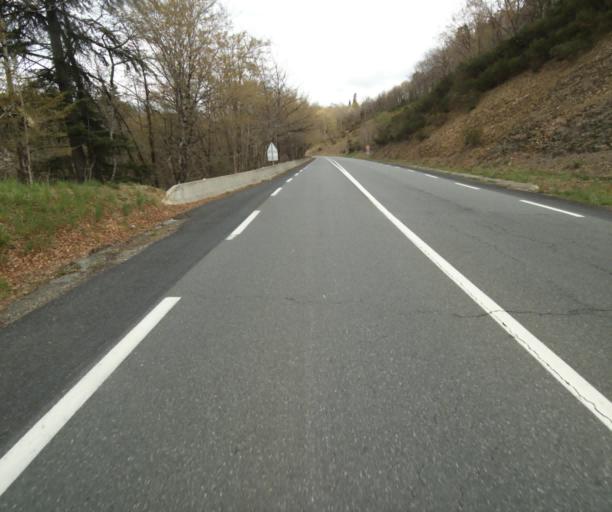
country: FR
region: Limousin
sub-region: Departement de la Correze
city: Sainte-Fortunade
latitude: 45.1899
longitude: 1.8428
